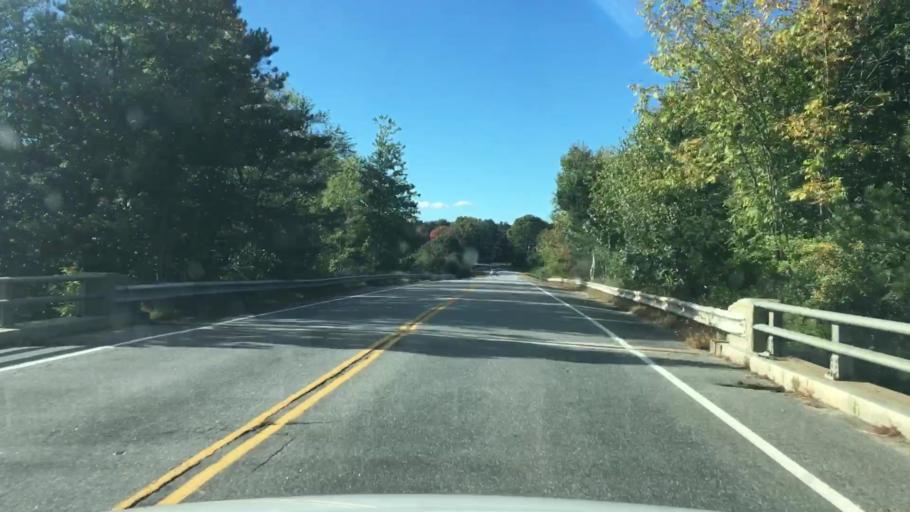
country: US
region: Maine
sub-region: Sagadahoc County
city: Topsham
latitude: 43.9281
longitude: -69.9998
